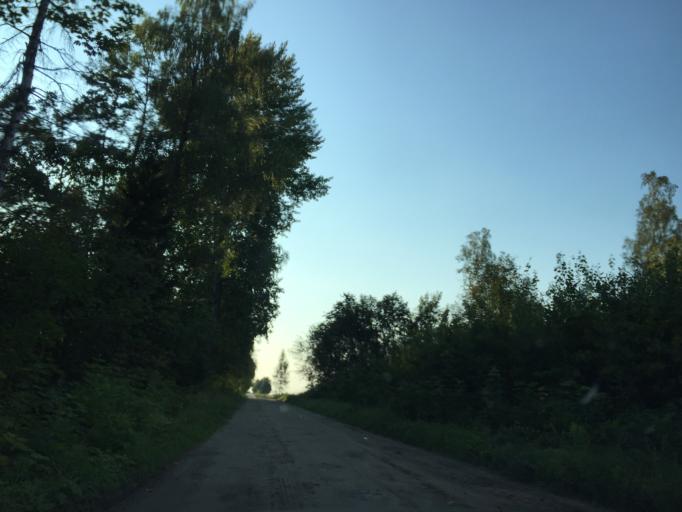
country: LV
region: Limbazu Rajons
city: Limbazi
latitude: 57.5568
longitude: 24.7681
